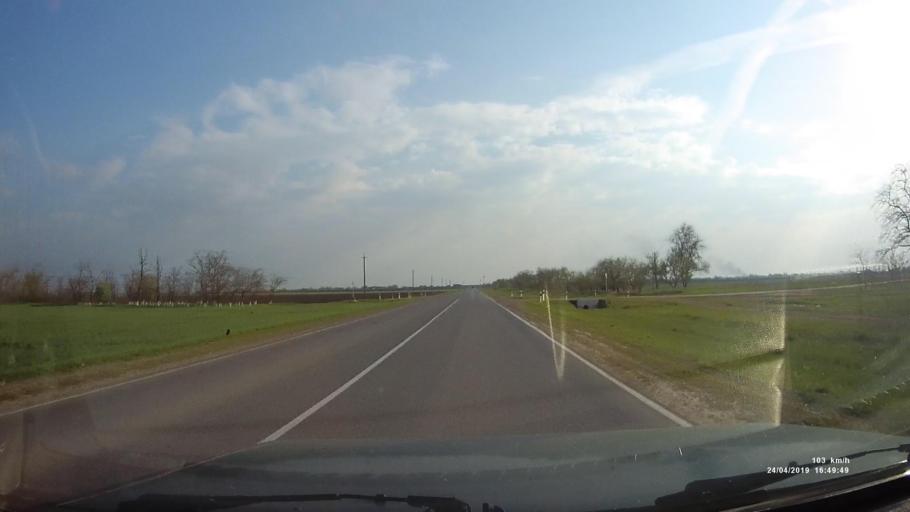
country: RU
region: Rostov
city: Proletarsk
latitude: 46.7122
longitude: 41.7600
